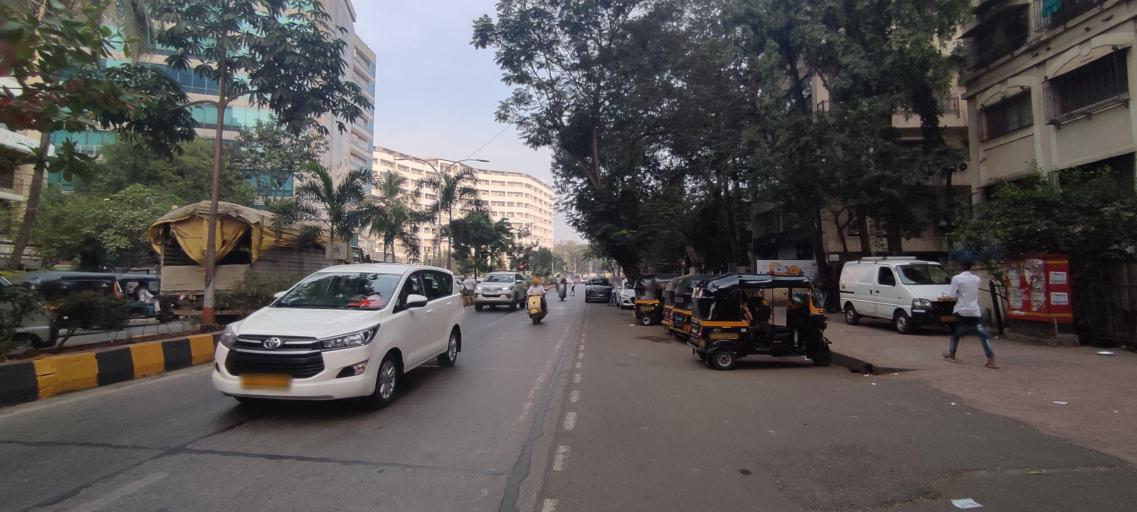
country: IN
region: Maharashtra
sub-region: Mumbai Suburban
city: Mumbai
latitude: 19.1028
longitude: 72.8354
